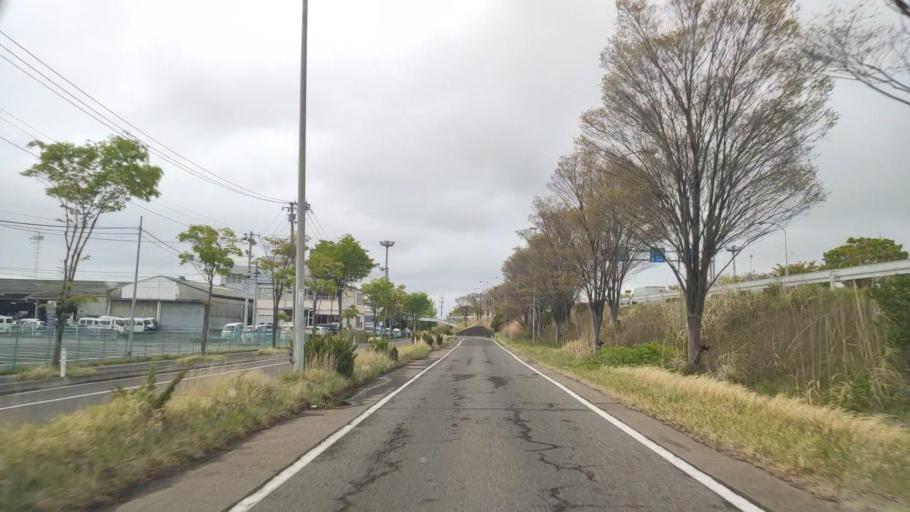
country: JP
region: Miyagi
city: Sendai-shi
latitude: 38.2661
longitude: 140.9380
